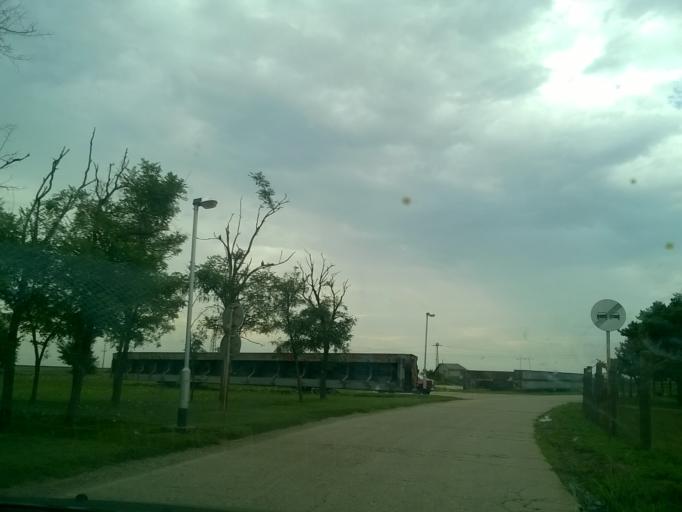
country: RS
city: Tomasevac
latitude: 45.2843
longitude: 20.6353
